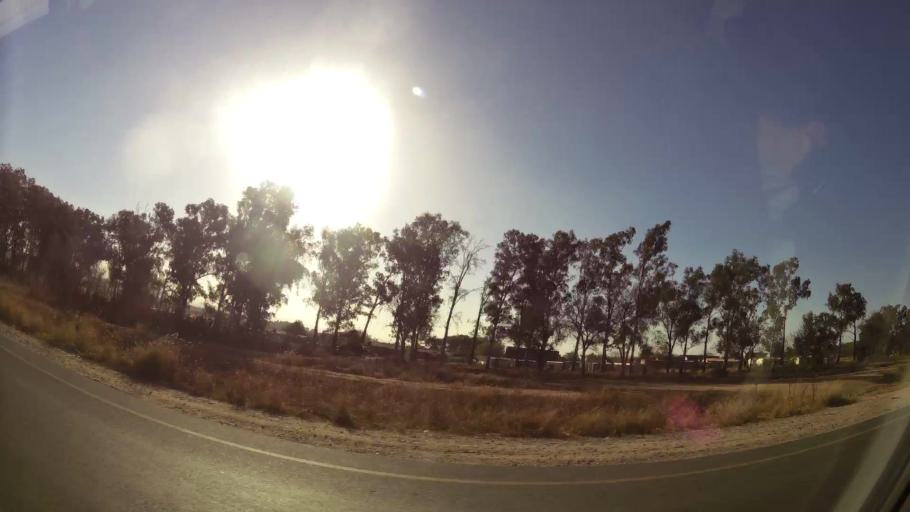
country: ZA
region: Gauteng
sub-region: City of Johannesburg Metropolitan Municipality
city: Diepsloot
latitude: -25.9396
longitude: 27.9848
